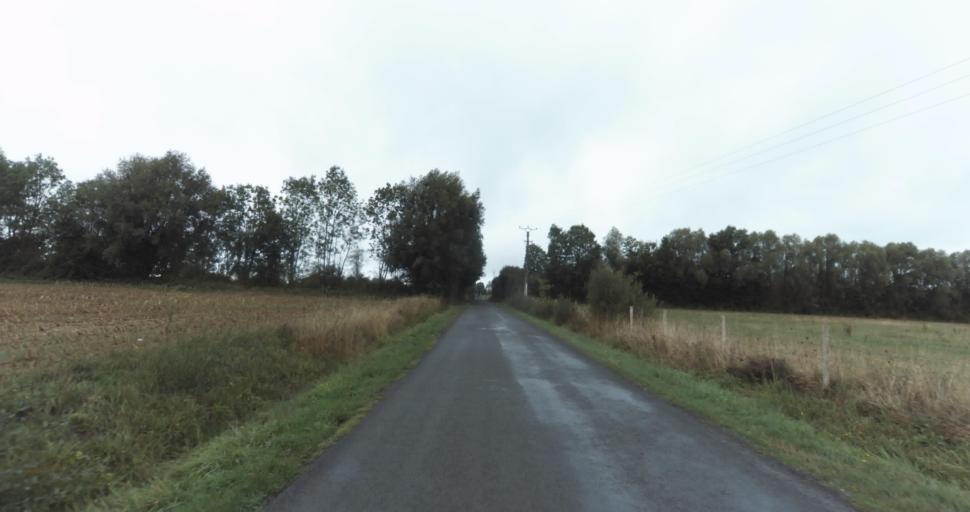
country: FR
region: Lower Normandy
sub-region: Departement de l'Orne
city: Sainte-Gauburge-Sainte-Colombe
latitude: 48.7457
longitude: 0.4373
